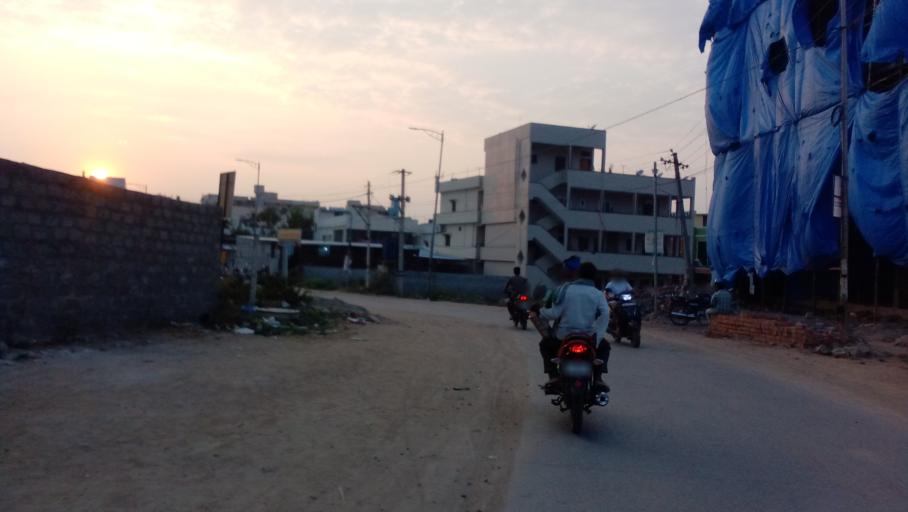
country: IN
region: Telangana
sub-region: Medak
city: Serilingampalle
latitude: 17.5224
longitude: 78.3014
